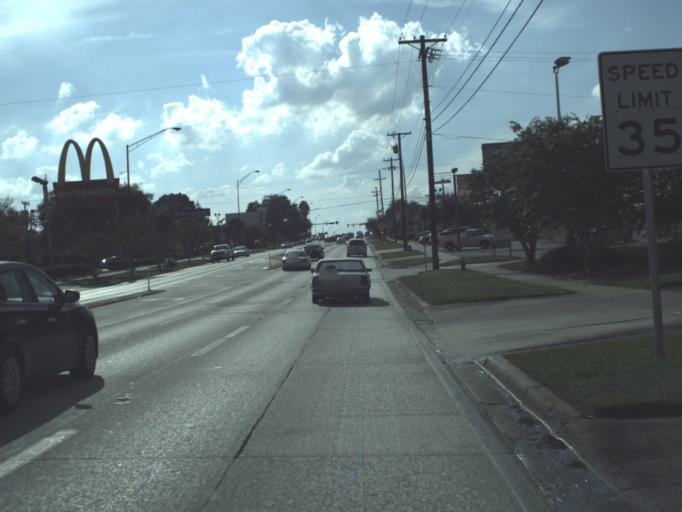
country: US
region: Florida
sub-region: Polk County
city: Lakeland
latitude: 28.0551
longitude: -81.9496
